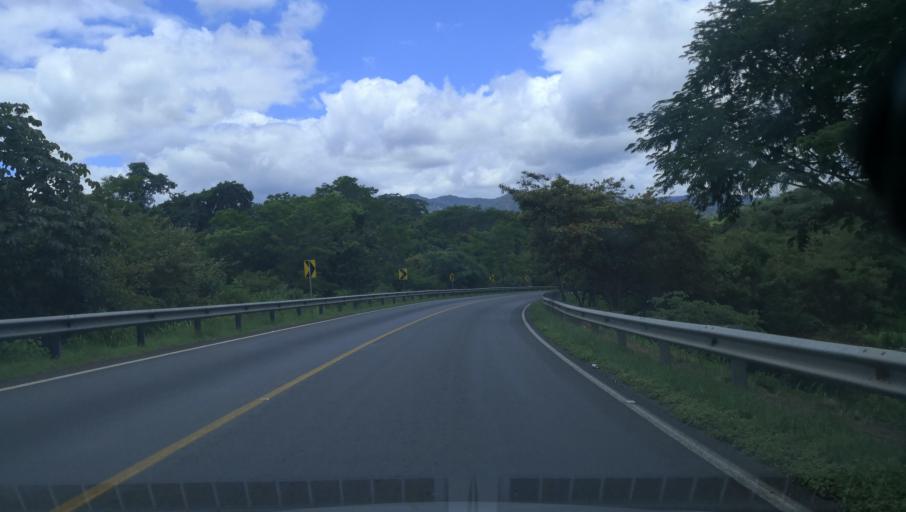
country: NI
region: Esteli
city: Condega
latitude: 13.2503
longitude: -86.3625
